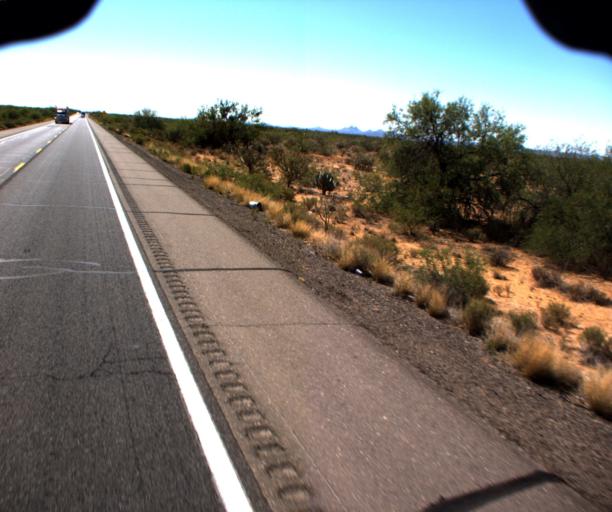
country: US
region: Arizona
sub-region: Yavapai County
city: Congress
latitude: 34.1082
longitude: -112.9288
